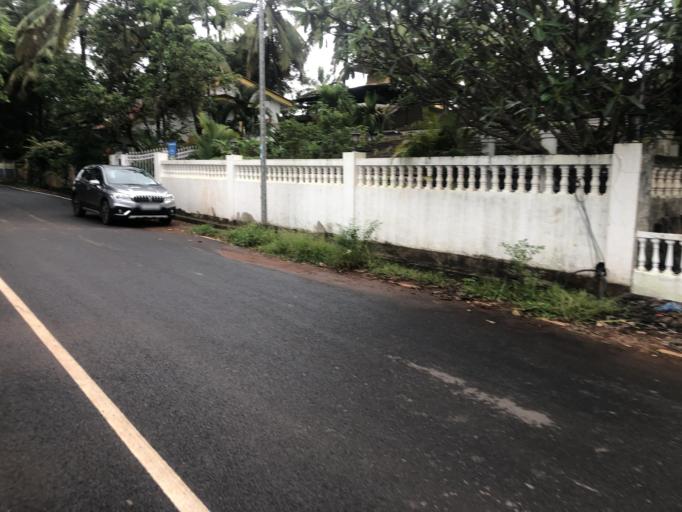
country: IN
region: Goa
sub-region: North Goa
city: Serula
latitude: 15.5356
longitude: 73.8276
